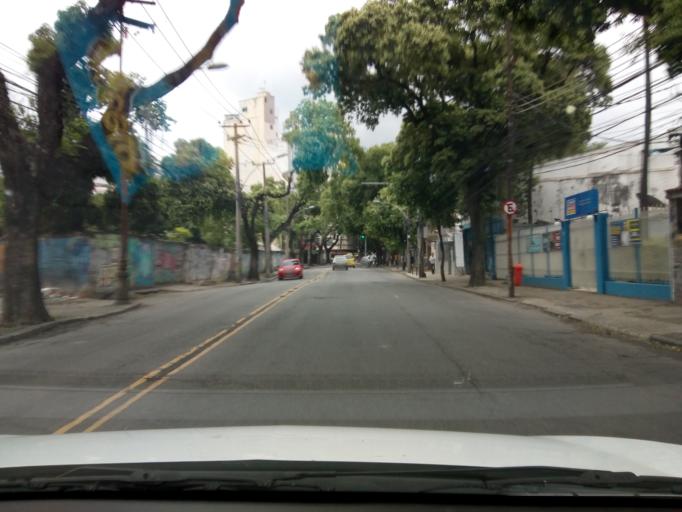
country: BR
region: Rio de Janeiro
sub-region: Rio De Janeiro
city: Rio de Janeiro
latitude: -22.9214
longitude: -43.2288
